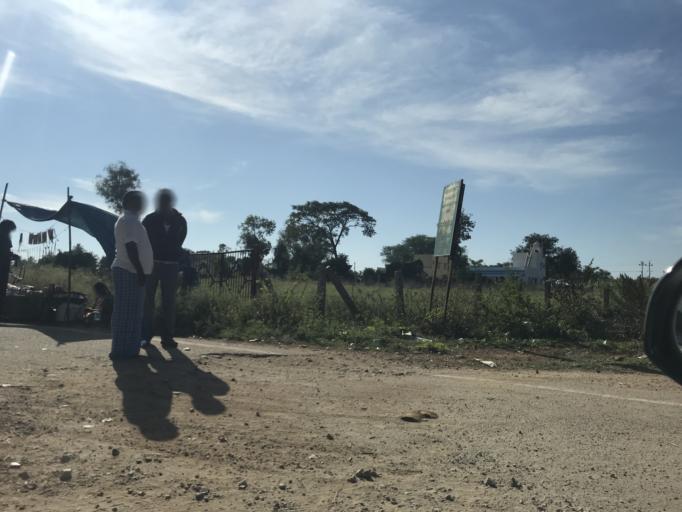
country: IN
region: Karnataka
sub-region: Mysore
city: Mysore
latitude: 12.2193
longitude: 76.5725
